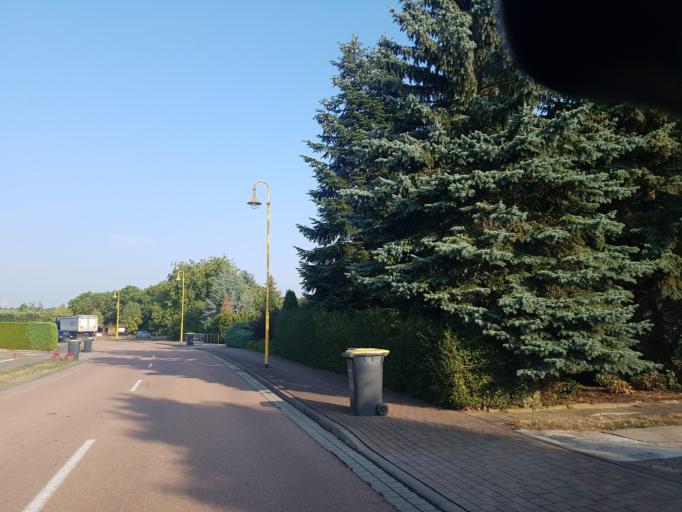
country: DE
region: Saxony-Anhalt
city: Nudersdorf
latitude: 51.9639
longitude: 12.5278
